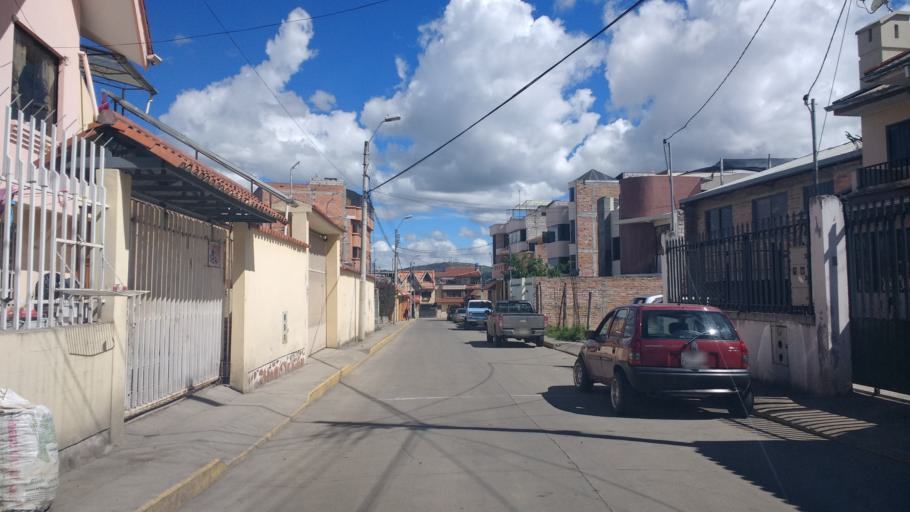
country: EC
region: Azuay
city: Cuenca
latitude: -2.8966
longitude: -79.0345
